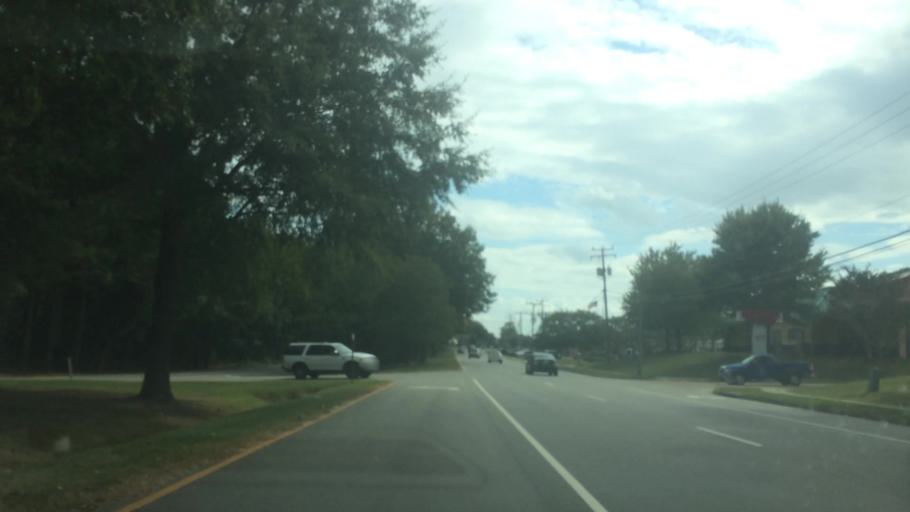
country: US
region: Virginia
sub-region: James City County
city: Williamsburg
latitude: 37.3058
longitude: -76.7293
